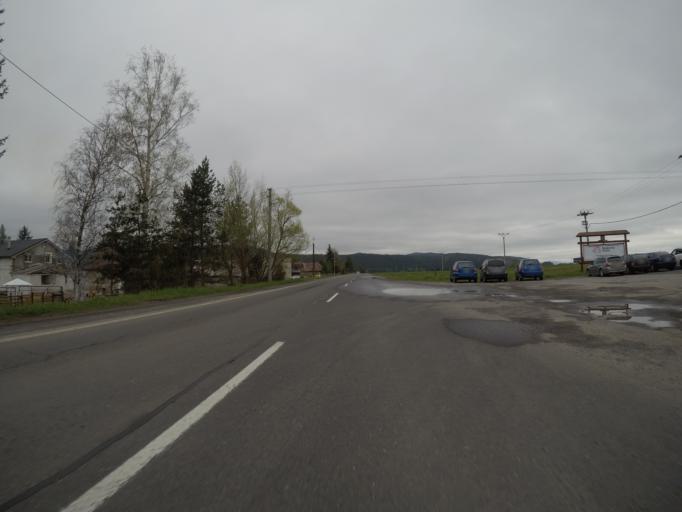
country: SK
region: Presovsky
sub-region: Okres Poprad
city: Strba
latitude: 49.0667
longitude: 19.9854
